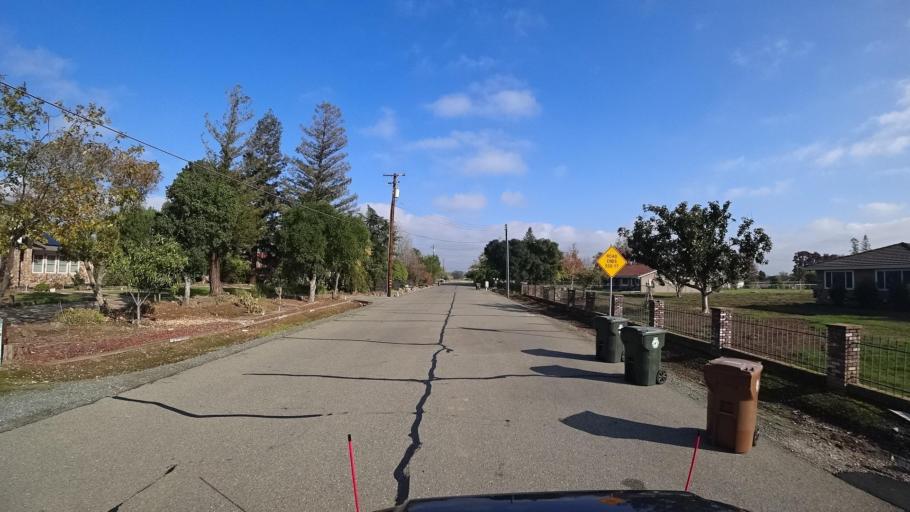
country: US
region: California
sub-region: Sacramento County
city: Vineyard
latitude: 38.4442
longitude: -121.3554
